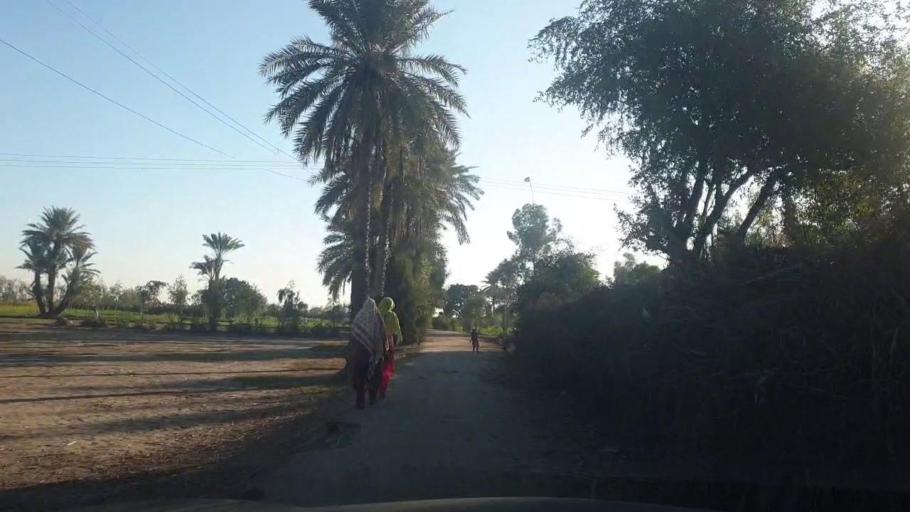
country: PK
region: Sindh
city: Ghotki
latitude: 27.9925
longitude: 69.2609
